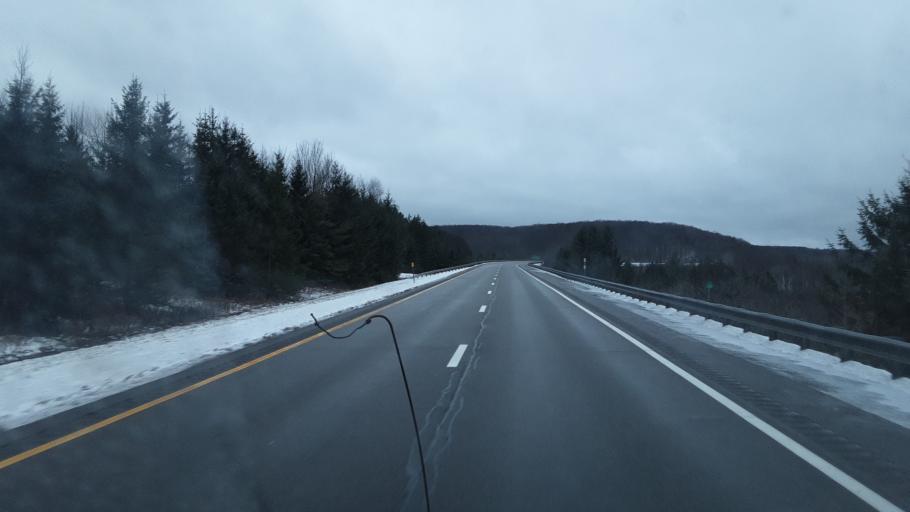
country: US
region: New York
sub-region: Allegany County
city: Alfred
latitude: 42.3191
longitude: -77.8375
